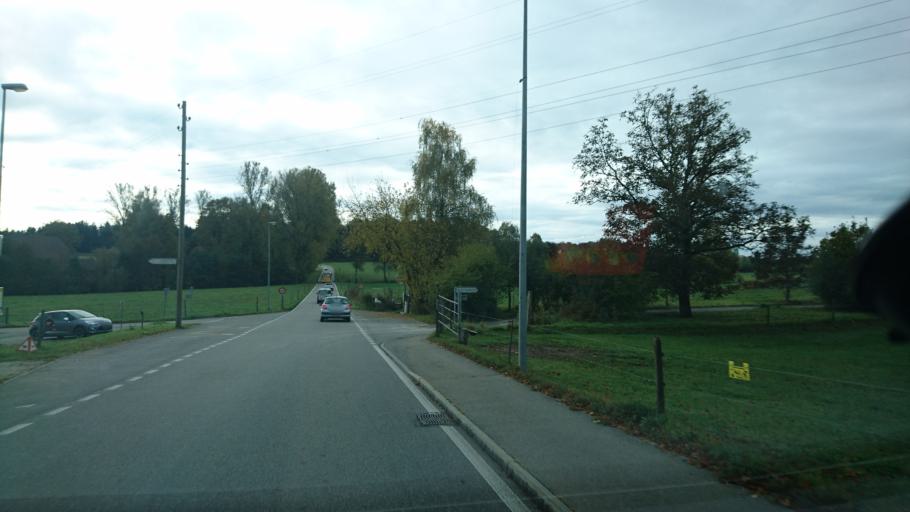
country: CH
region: Bern
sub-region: Bern-Mittelland District
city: Kirchlindach
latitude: 46.9937
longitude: 7.4120
